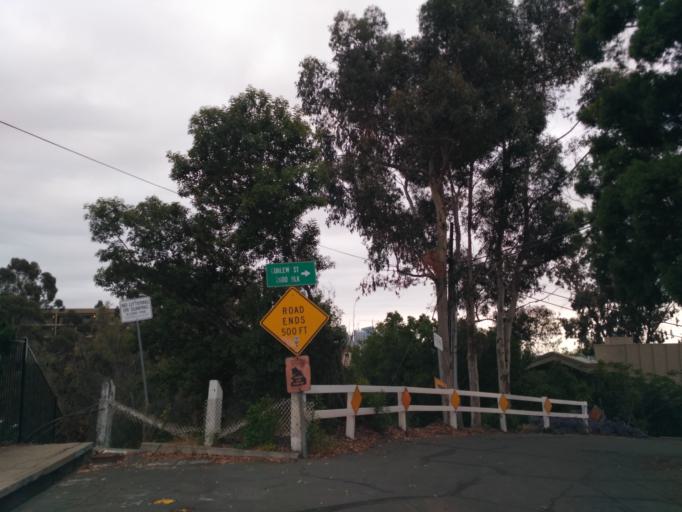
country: US
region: California
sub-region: San Diego County
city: San Diego
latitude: 32.7337
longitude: -117.1667
